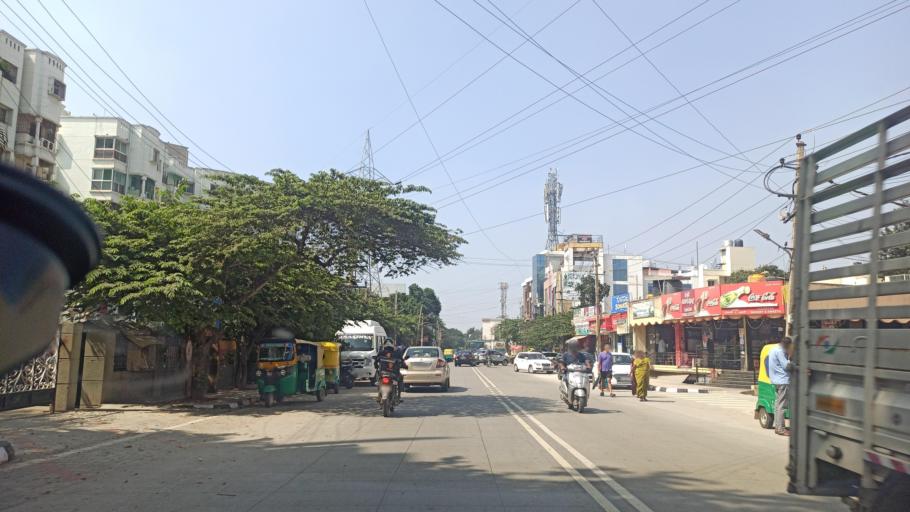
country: IN
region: Karnataka
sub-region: Bangalore Urban
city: Yelahanka
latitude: 13.0578
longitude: 77.5886
